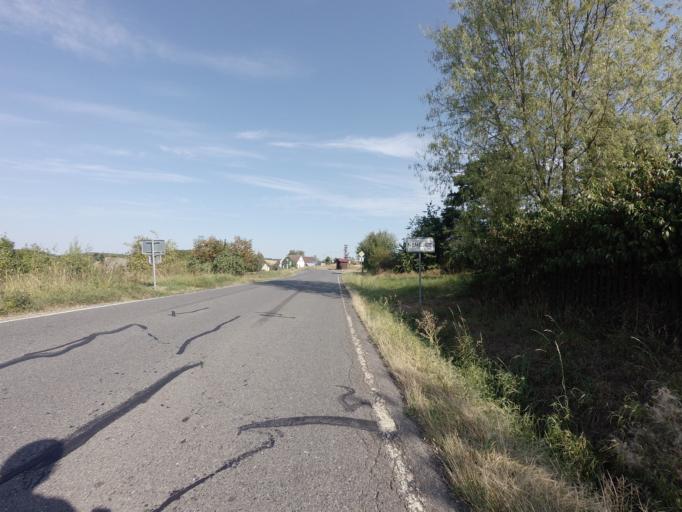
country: CZ
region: Jihocesky
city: Bernartice
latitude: 49.3253
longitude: 14.3596
